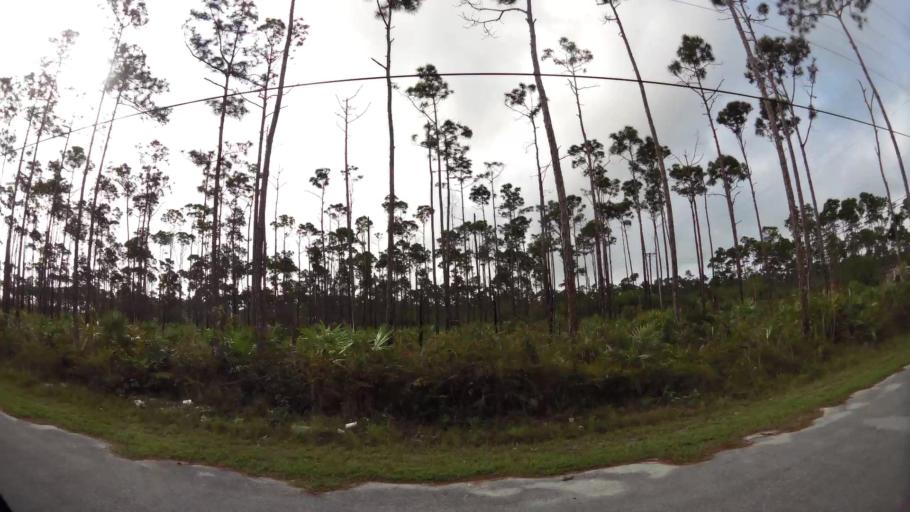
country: BS
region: Freeport
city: Freeport
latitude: 26.5360
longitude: -78.7087
